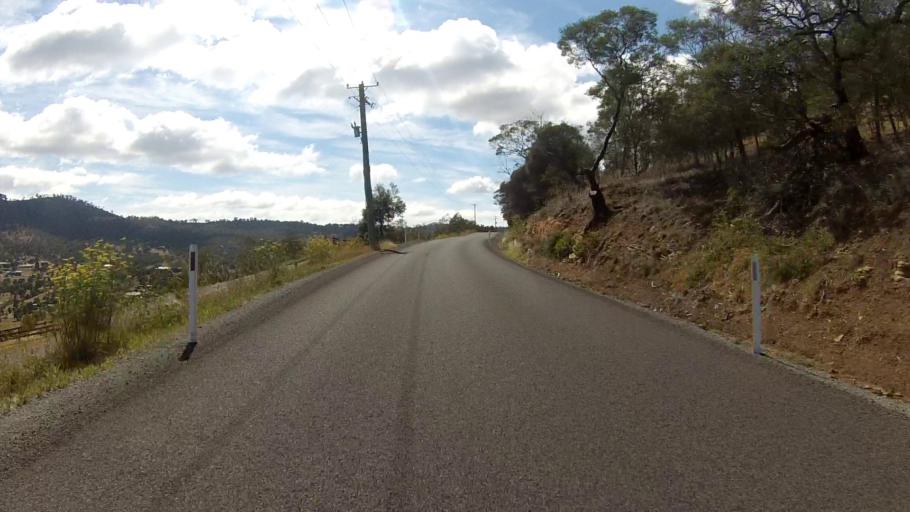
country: AU
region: Tasmania
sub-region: Glenorchy
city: Austins Ferry
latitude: -42.7280
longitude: 147.2798
